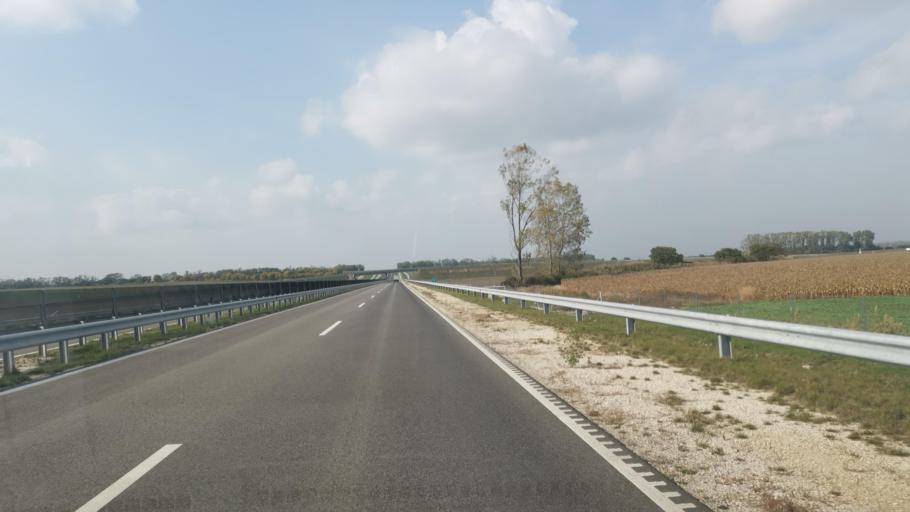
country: HU
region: Gyor-Moson-Sopron
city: Nagycenk
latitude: 47.5776
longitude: 16.7665
